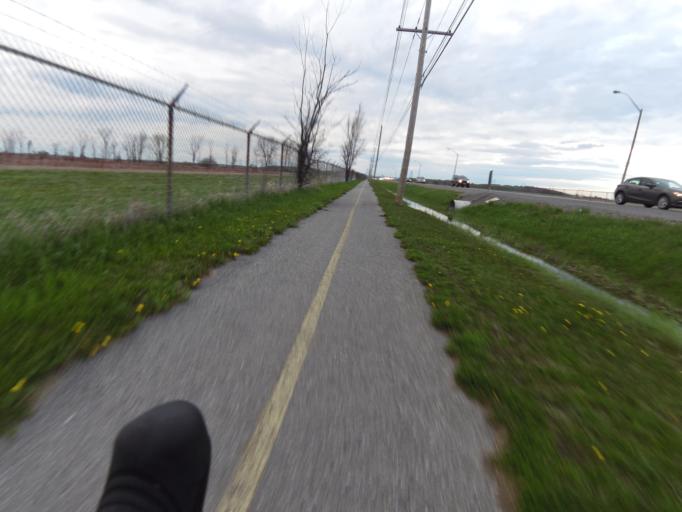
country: CA
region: Ontario
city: Bells Corners
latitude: 45.3005
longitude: -75.7646
